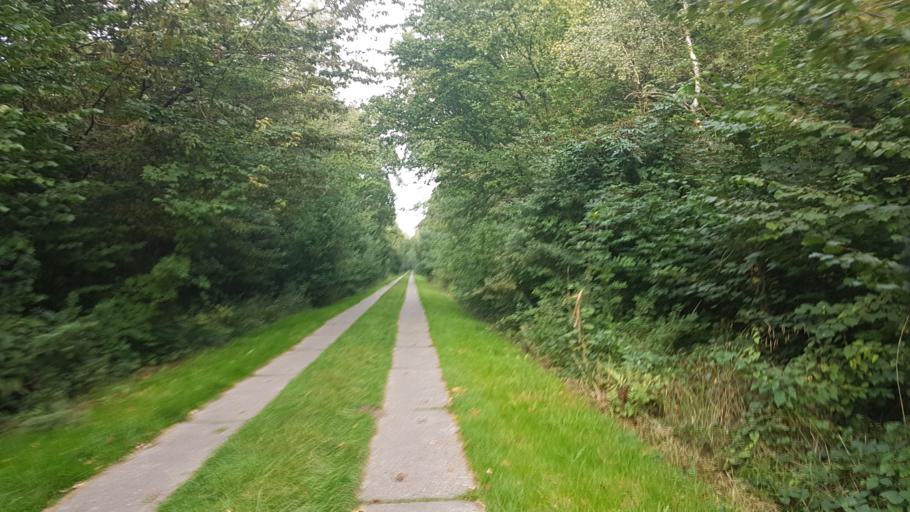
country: DE
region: Mecklenburg-Vorpommern
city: Gingst
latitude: 54.4782
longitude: 13.1767
